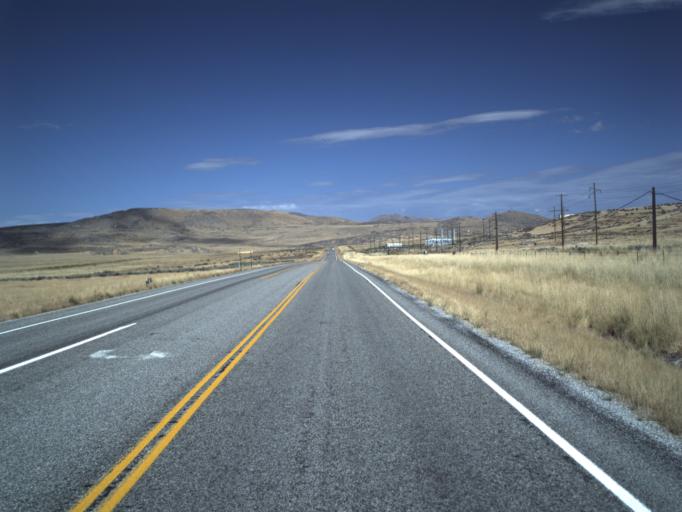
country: US
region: Utah
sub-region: Box Elder County
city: Tremonton
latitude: 41.6394
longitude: -112.4263
